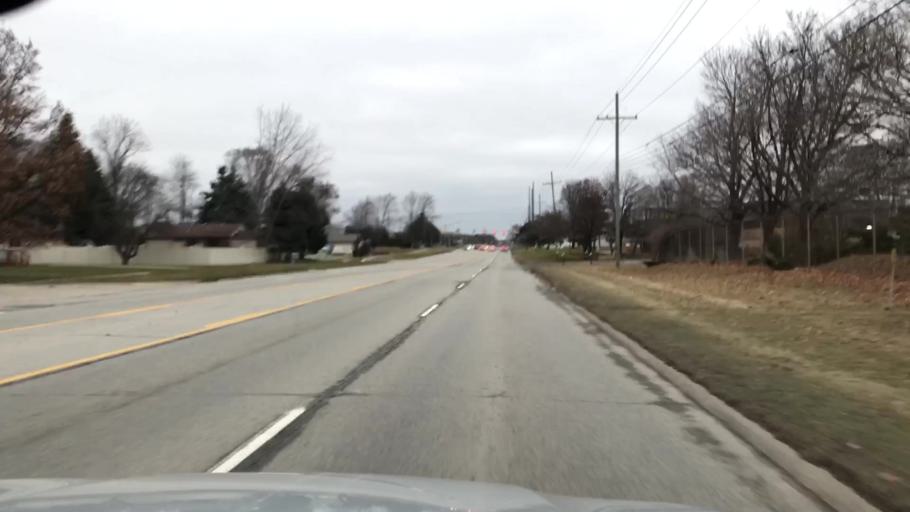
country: US
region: Michigan
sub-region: Wayne County
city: Westland
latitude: 42.3720
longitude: -83.4115
